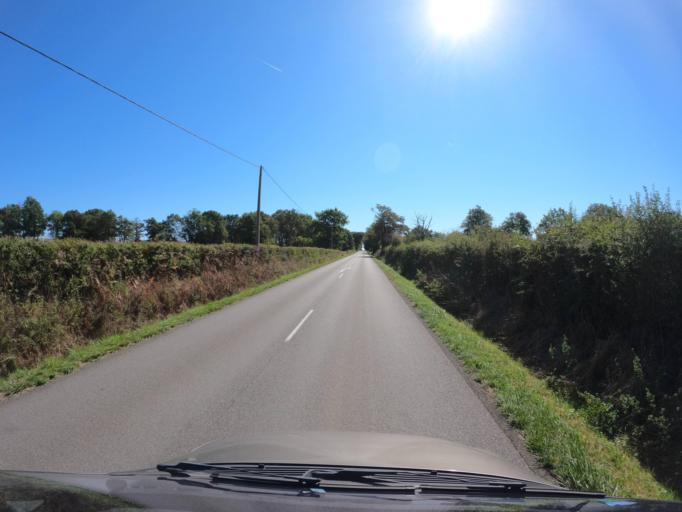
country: FR
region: Limousin
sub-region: Departement de la Haute-Vienne
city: Le Dorat
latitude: 46.2681
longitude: 1.0275
